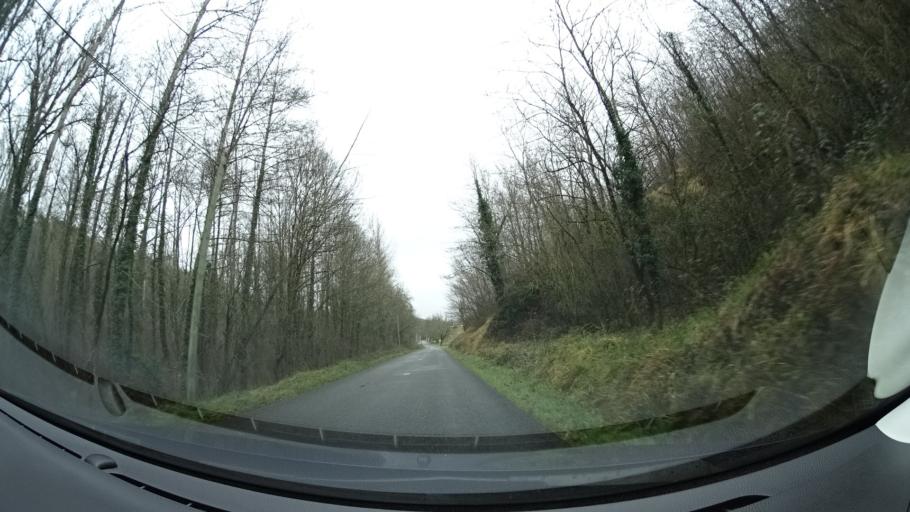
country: FR
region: Midi-Pyrenees
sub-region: Departement du Lot
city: Salviac
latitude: 44.5941
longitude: 1.2417
